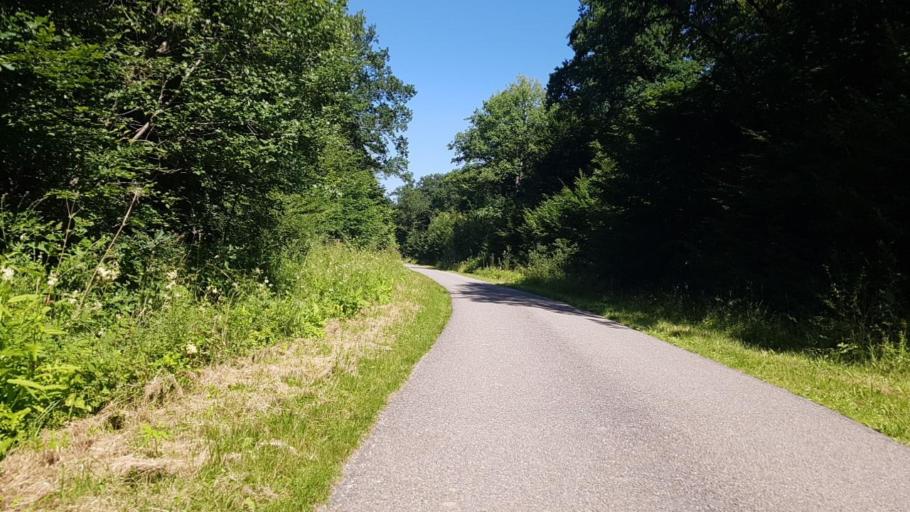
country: BE
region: Wallonia
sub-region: Province du Hainaut
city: Momignies
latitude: 50.0902
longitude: 4.2289
